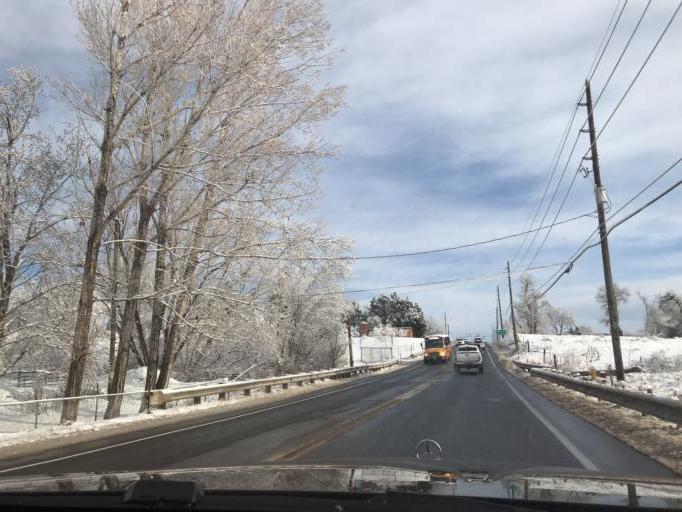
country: US
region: Colorado
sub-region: Jefferson County
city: Applewood
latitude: 39.8405
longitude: -105.1652
